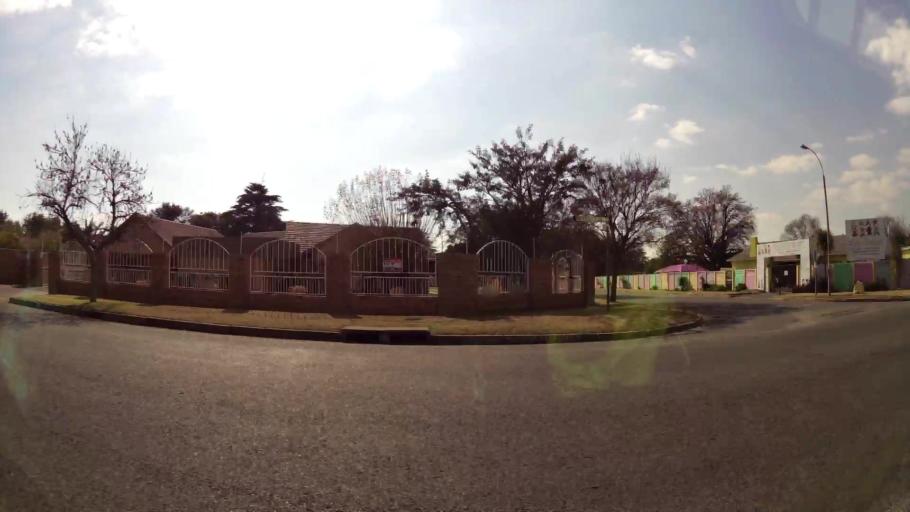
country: ZA
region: Gauteng
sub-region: City of Johannesburg Metropolitan Municipality
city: Modderfontein
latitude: -26.0915
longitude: 28.2395
